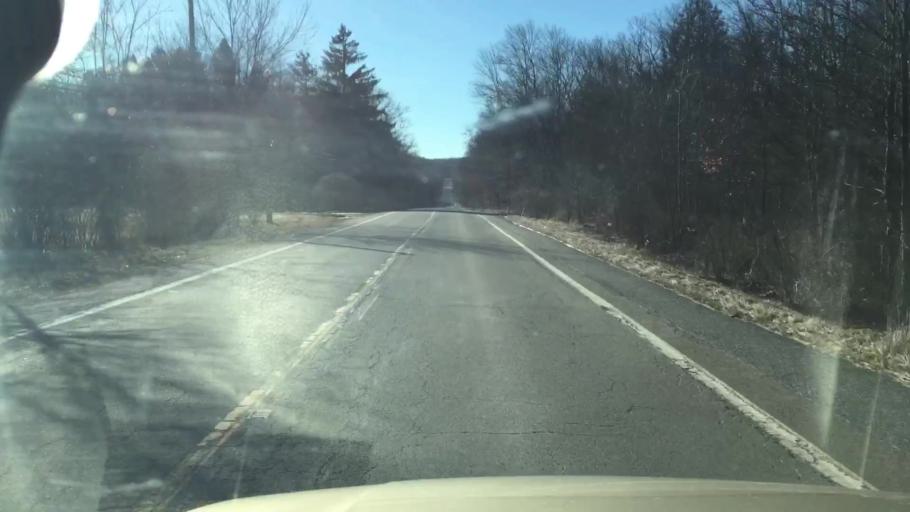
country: US
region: Pennsylvania
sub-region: Luzerne County
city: Freeland
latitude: 41.0337
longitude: -75.8501
